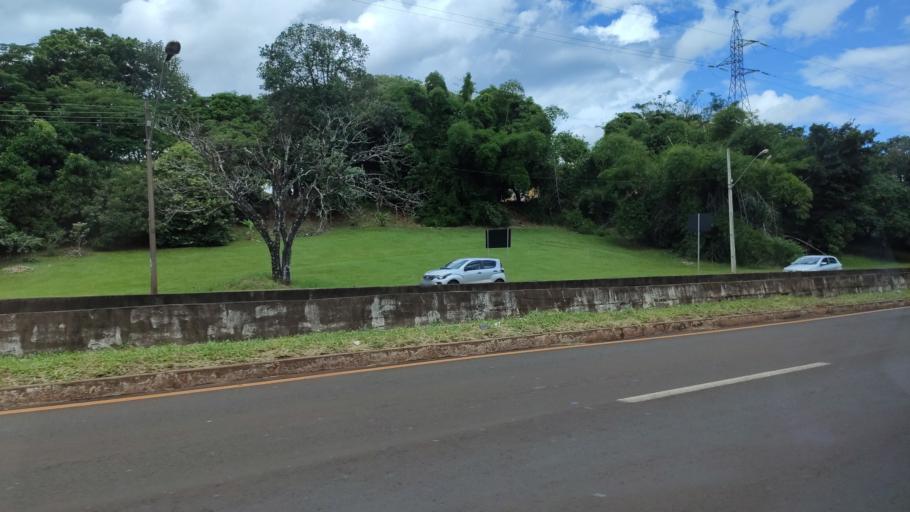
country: BR
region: Parana
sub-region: Londrina
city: Londrina
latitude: -23.3238
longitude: -51.1476
